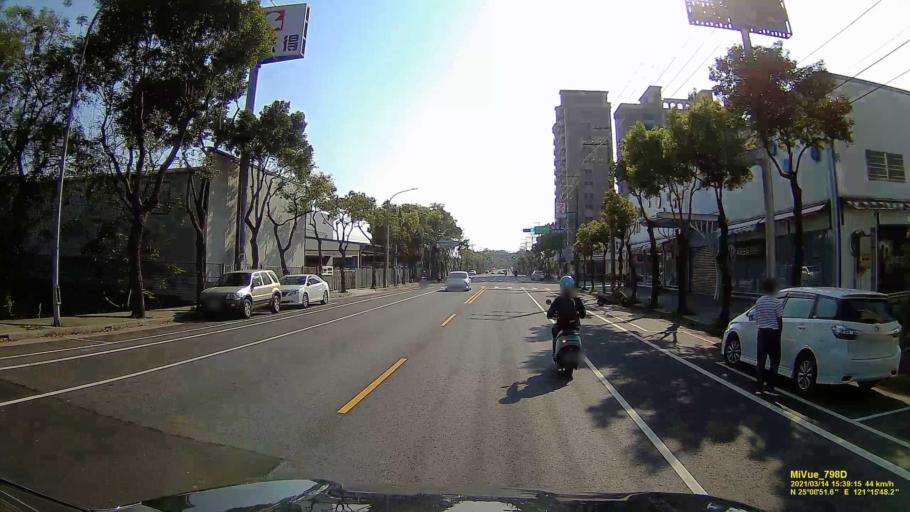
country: TW
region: Taiwan
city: Taoyuan City
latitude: 25.0142
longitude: 121.2632
